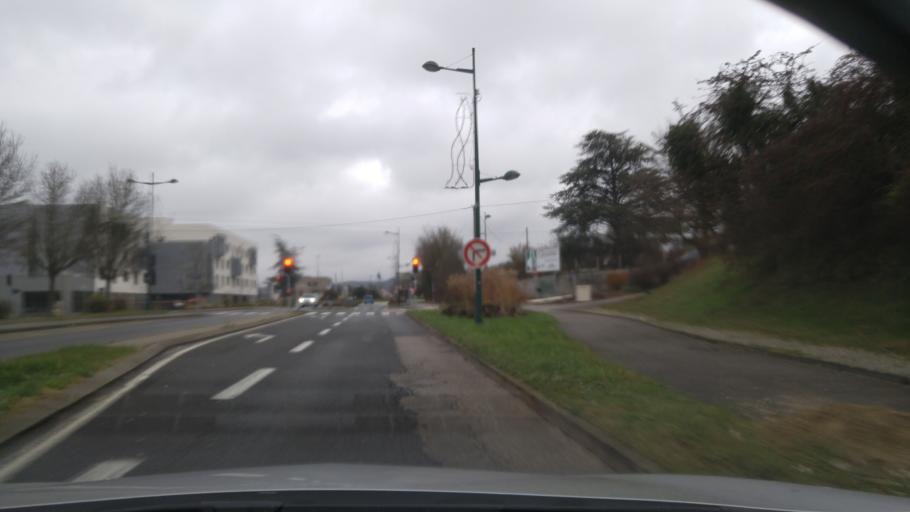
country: FR
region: Rhone-Alpes
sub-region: Departement de l'Isere
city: Villefontaine
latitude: 45.6138
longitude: 5.1513
